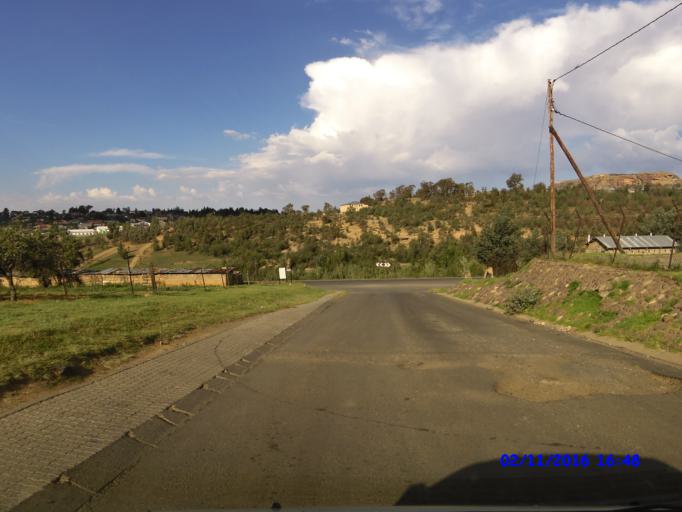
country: LS
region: Butha-Buthe
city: Butha-Buthe
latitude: -28.7612
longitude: 28.2488
